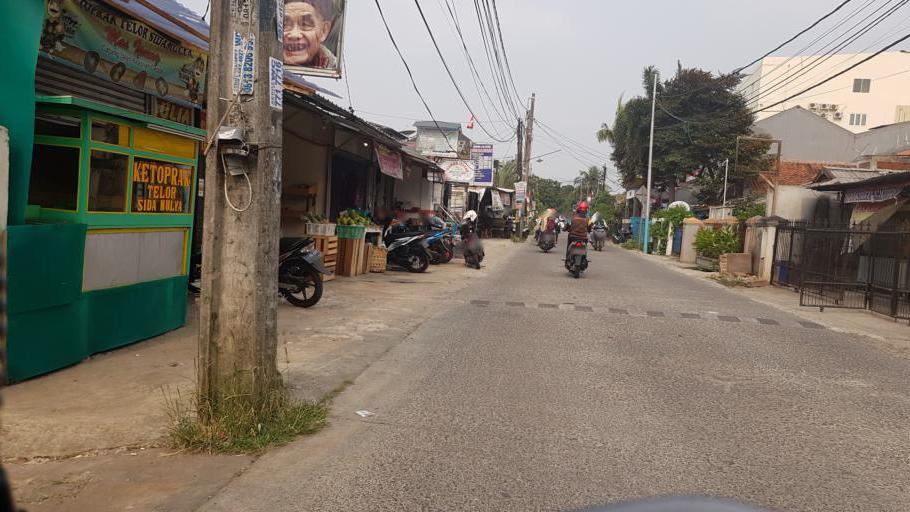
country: ID
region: West Java
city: Depok
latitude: -6.3726
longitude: 106.8429
